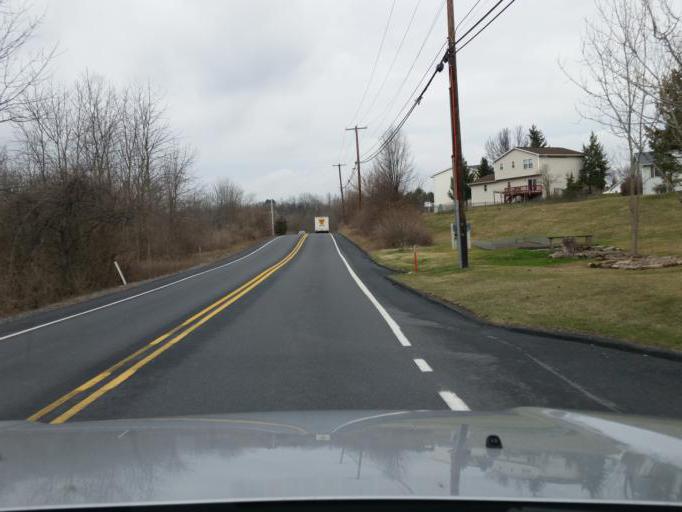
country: US
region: Pennsylvania
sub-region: Dauphin County
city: Paxtonia
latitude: 40.3053
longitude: -76.7668
